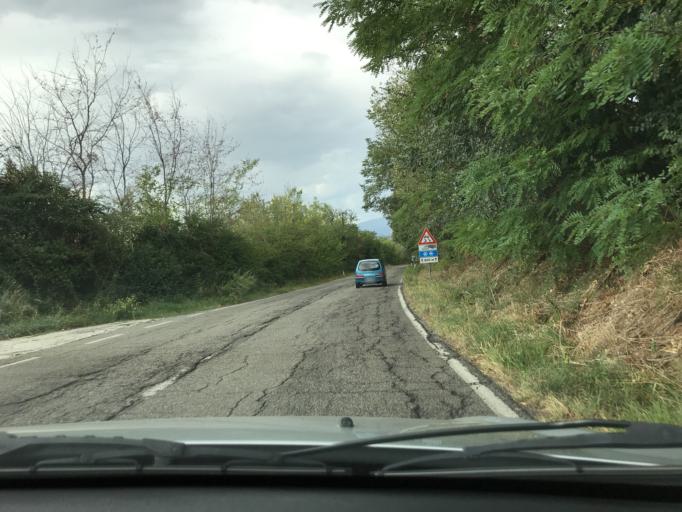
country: IT
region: Umbria
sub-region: Provincia di Terni
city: Montecchio
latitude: 42.6459
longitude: 12.2805
